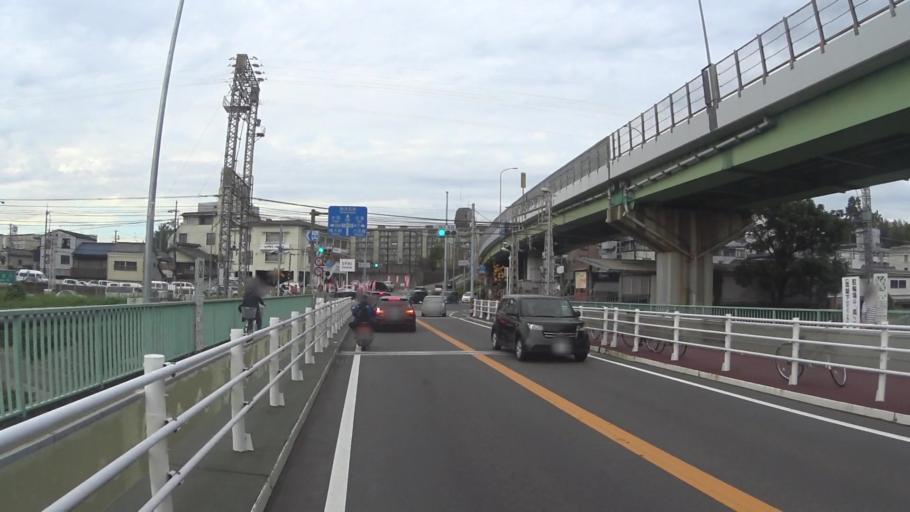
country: JP
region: Kyoto
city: Uji
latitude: 34.9274
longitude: 135.7683
